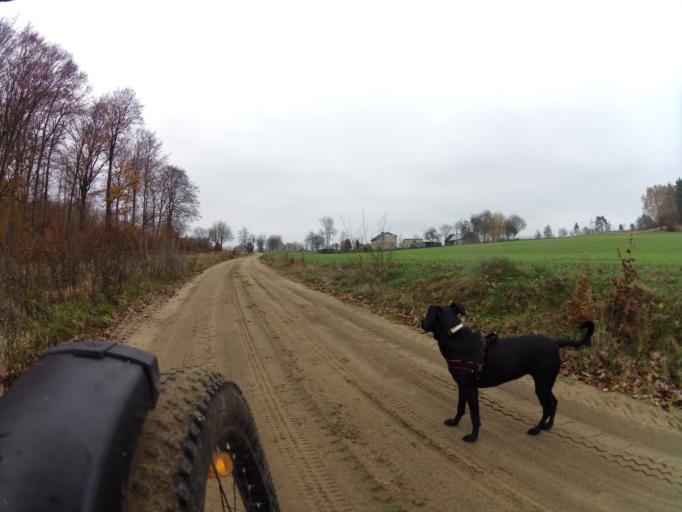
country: PL
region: Pomeranian Voivodeship
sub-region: Powiat pucki
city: Krokowa
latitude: 54.7160
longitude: 18.1390
